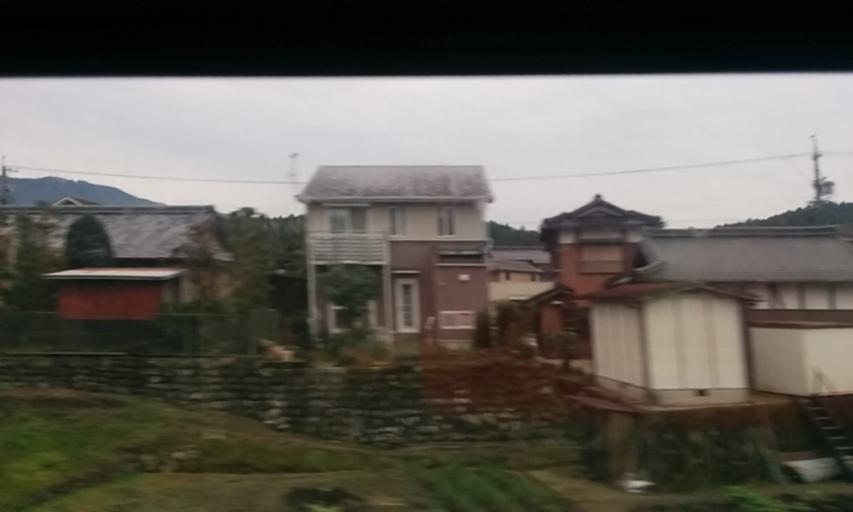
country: JP
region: Gifu
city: Nakatsugawa
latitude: 35.4774
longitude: 137.4635
